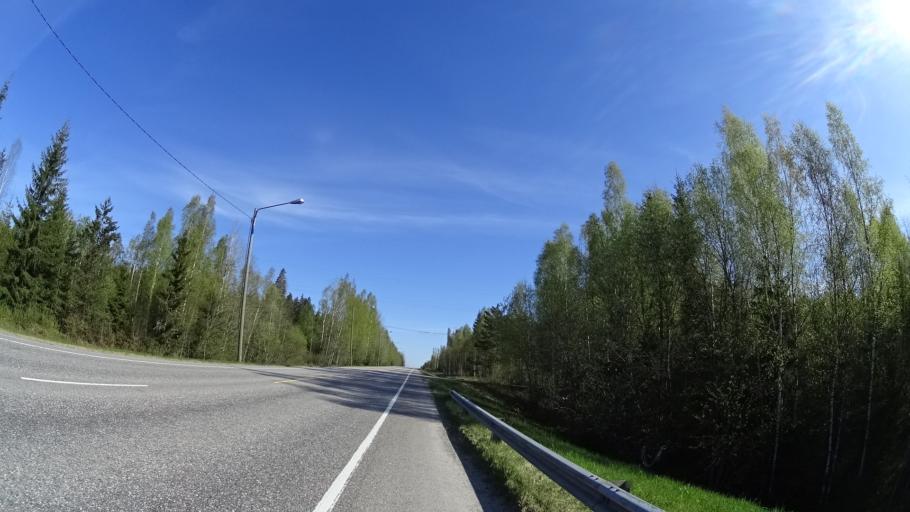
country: FI
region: Uusimaa
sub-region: Helsinki
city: Nurmijaervi
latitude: 60.3805
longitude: 24.8070
